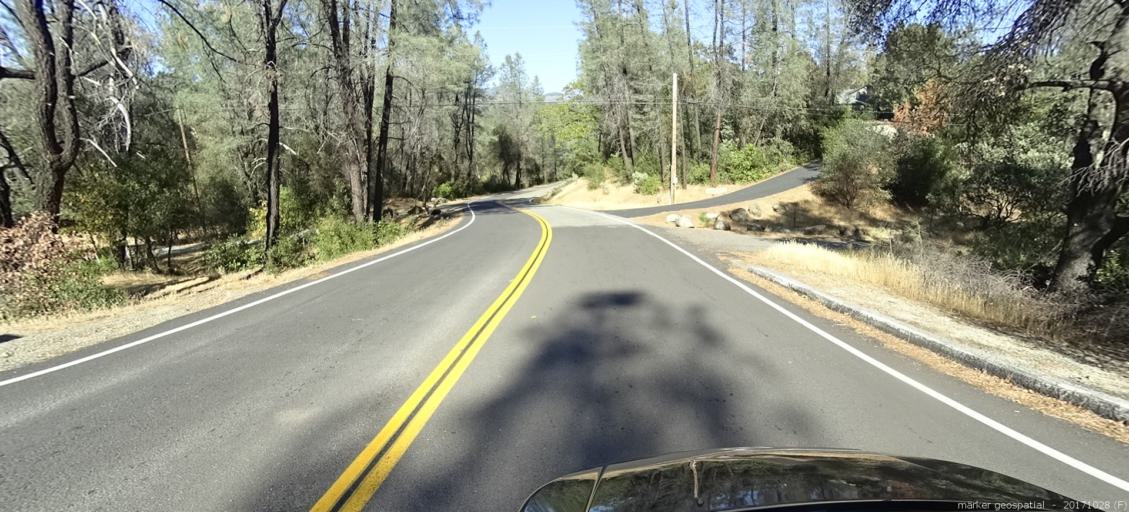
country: US
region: California
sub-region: Shasta County
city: Shasta
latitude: 40.6045
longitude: -122.5023
